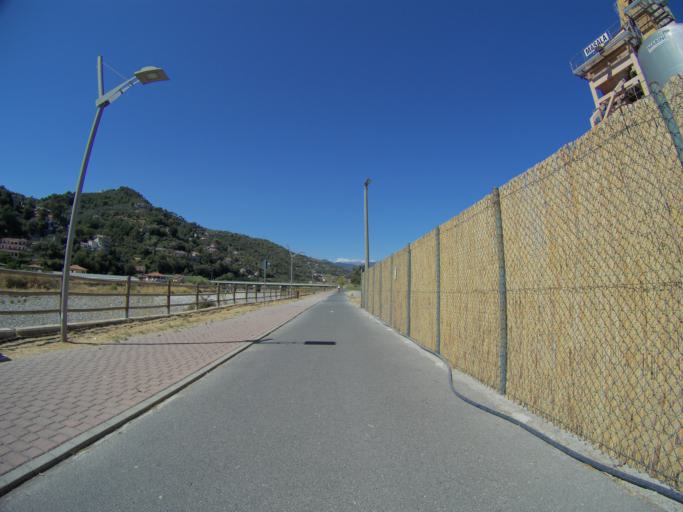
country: IT
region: Liguria
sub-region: Provincia di Imperia
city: Camporosso
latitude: 43.8023
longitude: 7.6271
